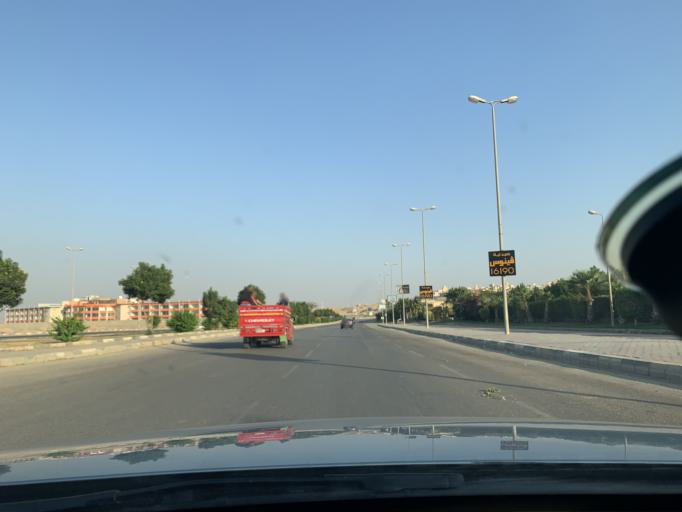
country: EG
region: Muhafazat al Qalyubiyah
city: Al Khankah
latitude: 30.0457
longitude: 31.5200
